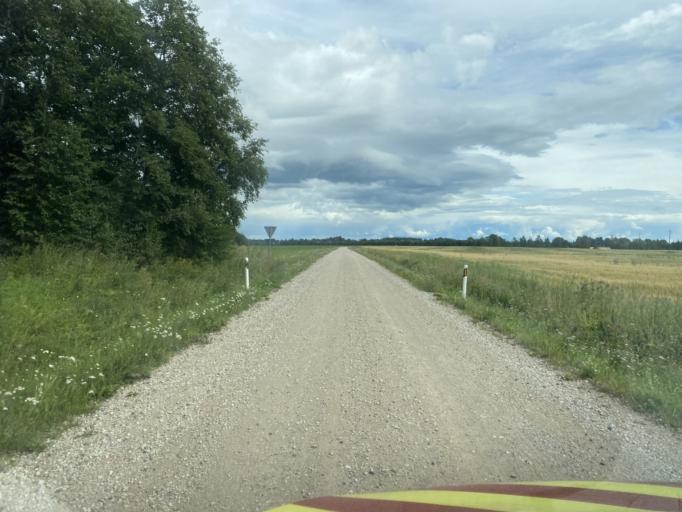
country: EE
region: Valgamaa
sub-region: Torva linn
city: Torva
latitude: 57.9393
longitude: 25.8842
